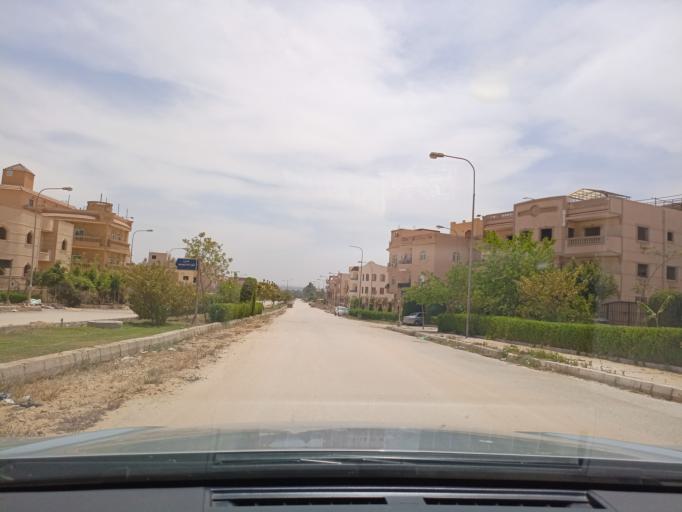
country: EG
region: Muhafazat al Qalyubiyah
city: Al Khankah
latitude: 30.2286
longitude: 31.4891
